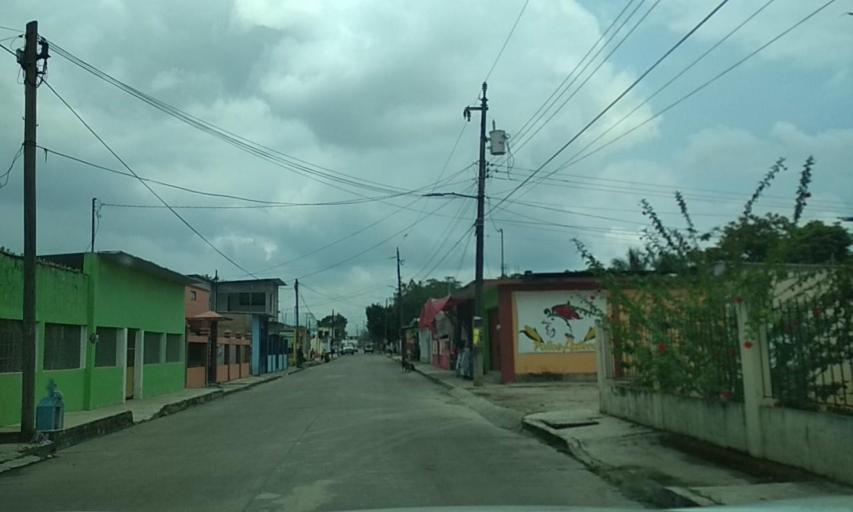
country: MX
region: Veracruz
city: Las Choapas
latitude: 17.8974
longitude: -94.0921
